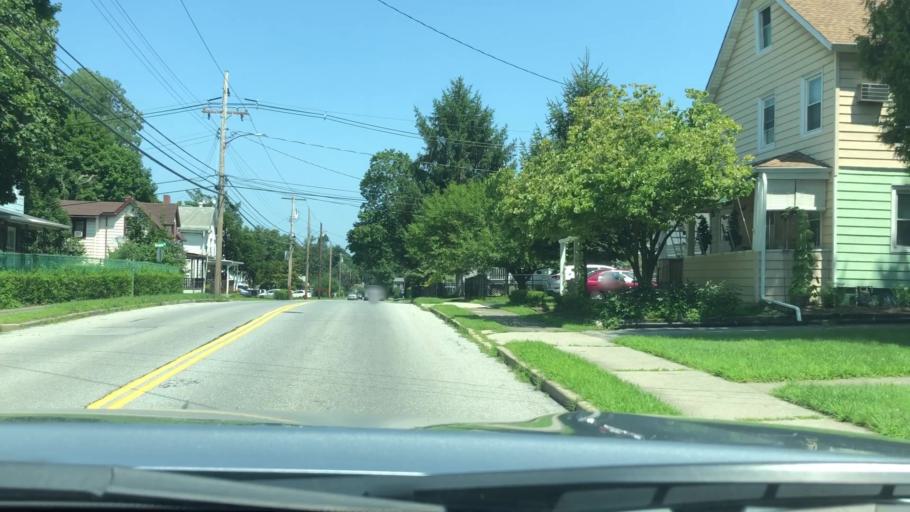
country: US
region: New York
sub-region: Dutchess County
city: Beacon
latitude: 41.5013
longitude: -73.9554
